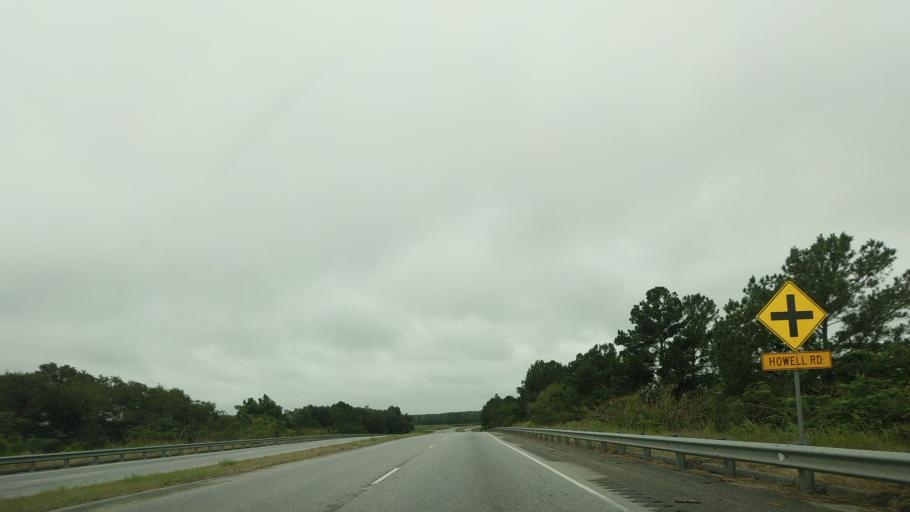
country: US
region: Georgia
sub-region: Lowndes County
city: Valdosta
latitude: 30.8292
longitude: -83.2283
